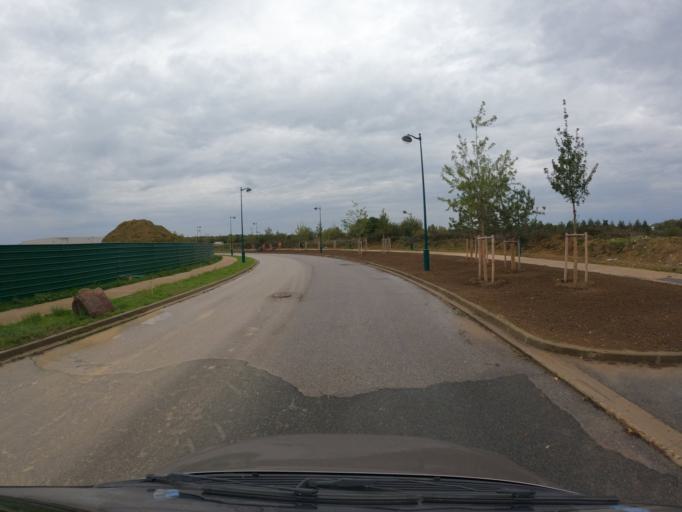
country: FR
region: Ile-de-France
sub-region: Departement de Seine-et-Marne
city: Serris
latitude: 48.8364
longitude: 2.7967
